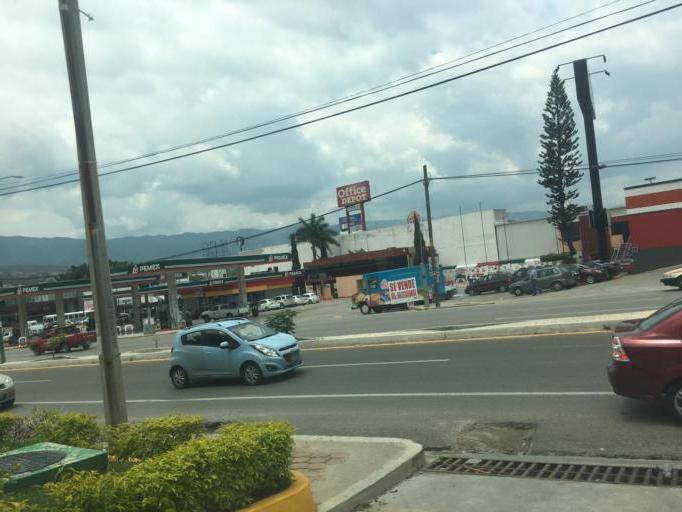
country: MX
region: Chiapas
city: Tuxtla Gutierrez
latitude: 16.7538
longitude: -93.1422
